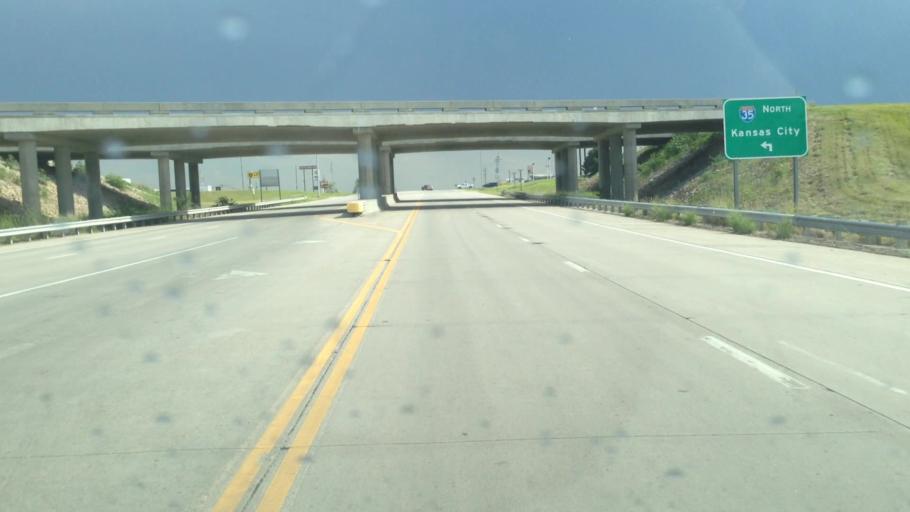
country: US
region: Kansas
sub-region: Osage County
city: Lyndon
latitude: 38.4299
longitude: -95.7286
